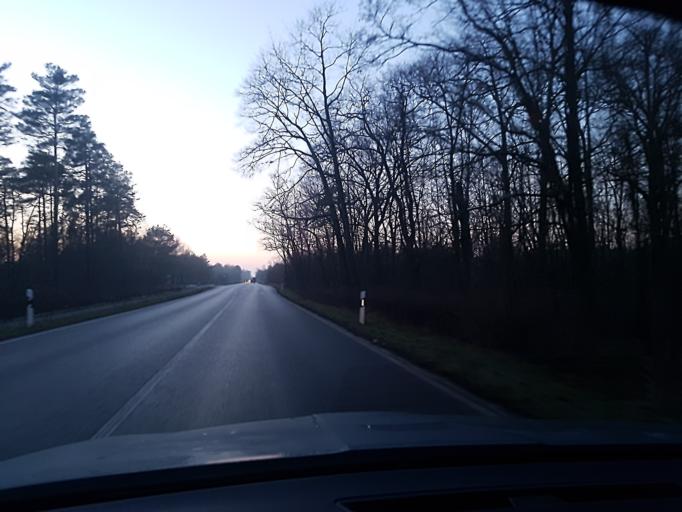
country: DE
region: Brandenburg
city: Schonewalde
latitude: 51.6351
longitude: 13.6331
